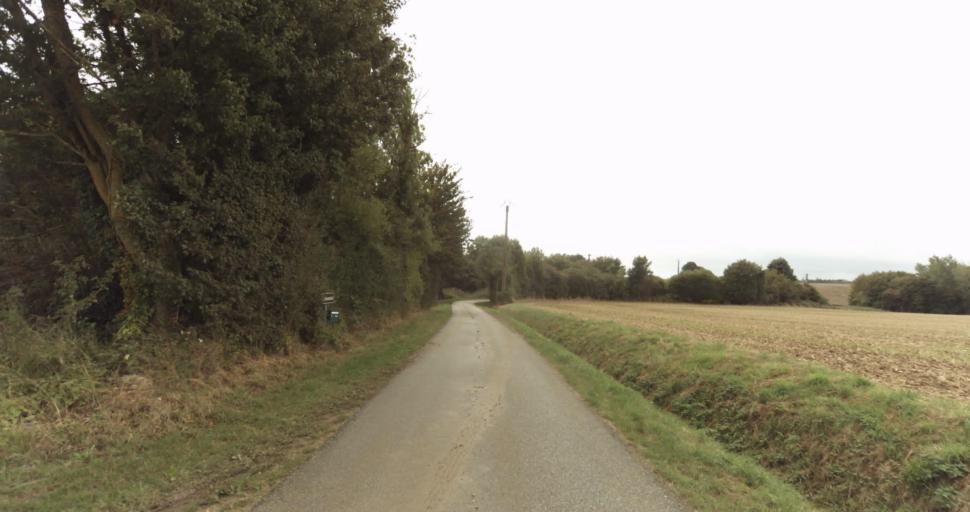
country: FR
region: Lower Normandy
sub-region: Departement de l'Orne
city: Sainte-Gauburge-Sainte-Colombe
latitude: 48.7391
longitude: 0.4545
